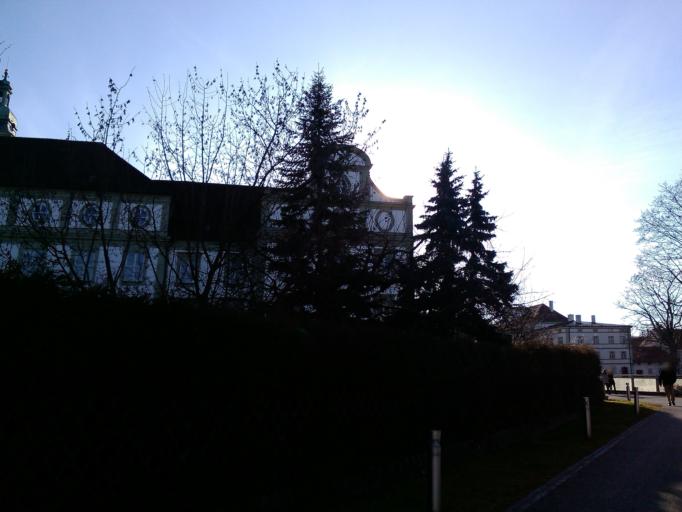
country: DE
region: Bavaria
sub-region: Upper Bavaria
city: Fuerstenfeldbruck
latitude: 48.1709
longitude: 11.2488
